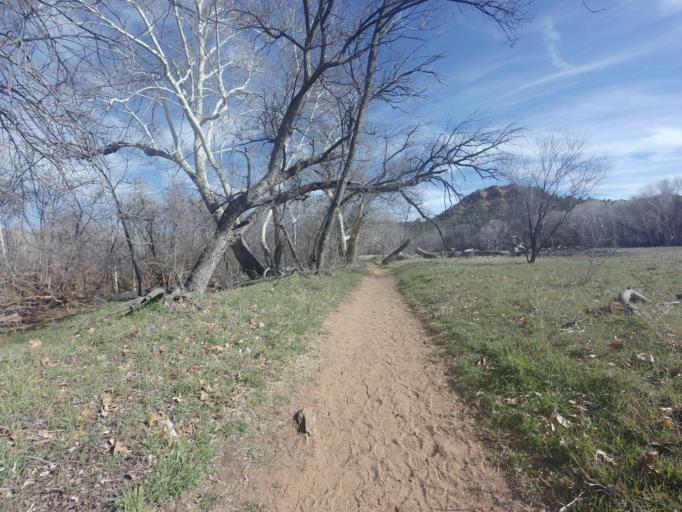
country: US
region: Arizona
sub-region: Yavapai County
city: West Sedona
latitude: 34.8102
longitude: -111.8312
